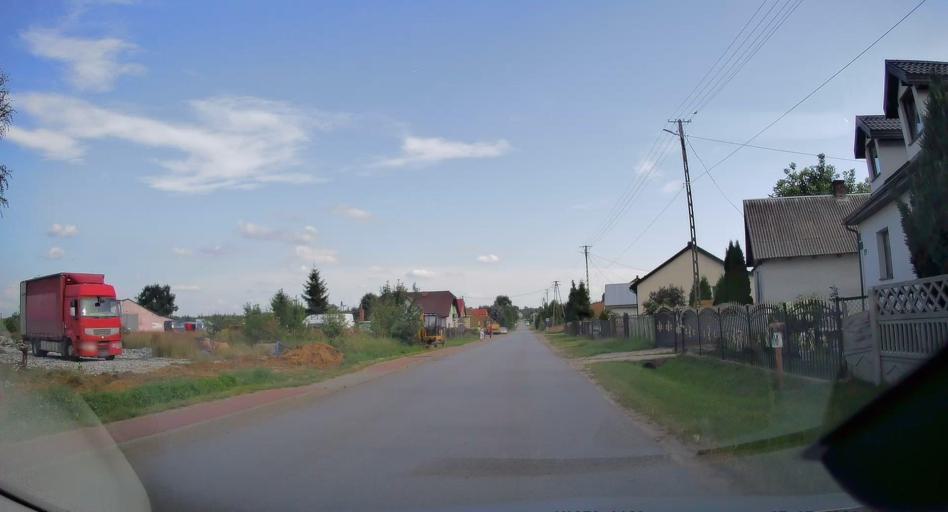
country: PL
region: Swietokrzyskie
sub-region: Powiat konecki
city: Gowarczow
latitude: 51.2786
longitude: 20.3705
